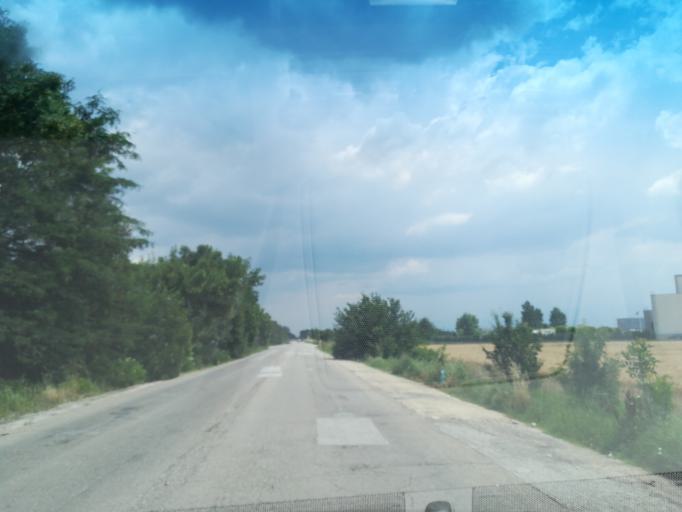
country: BG
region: Plovdiv
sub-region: Obshtina Plovdiv
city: Plovdiv
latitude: 42.1998
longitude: 24.6722
